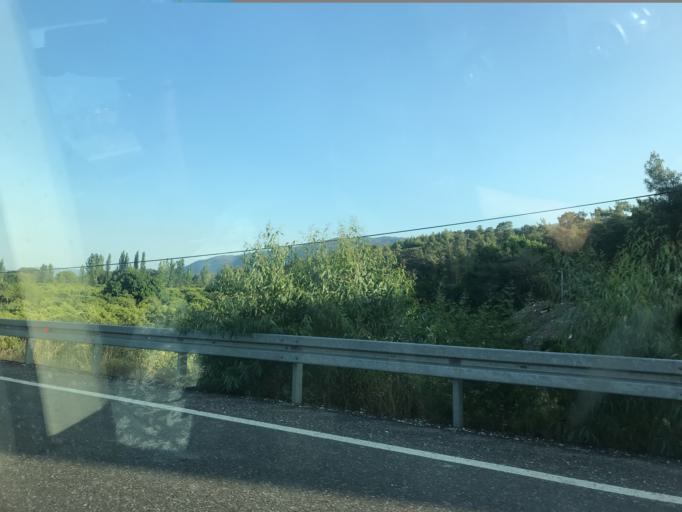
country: TR
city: Dalyan
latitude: 36.9864
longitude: 28.5919
